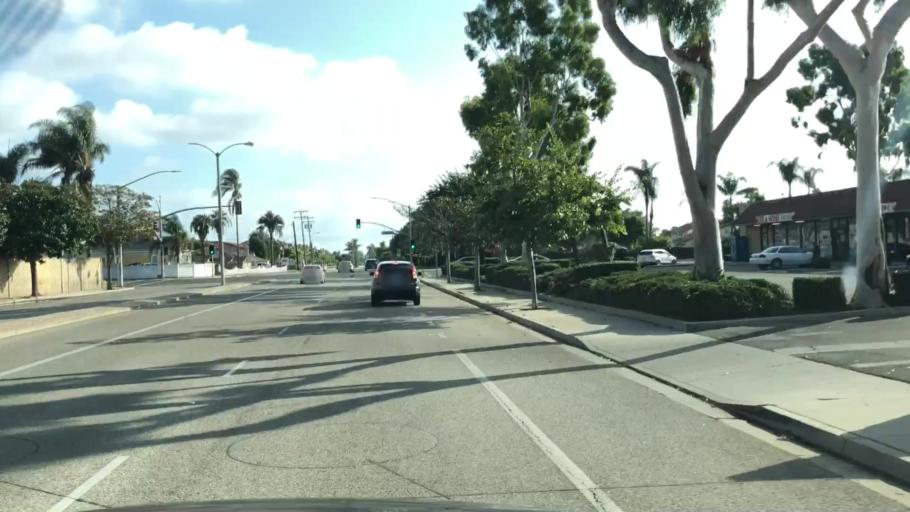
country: US
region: California
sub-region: Ventura County
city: Oxnard
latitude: 34.1912
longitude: -119.2081
